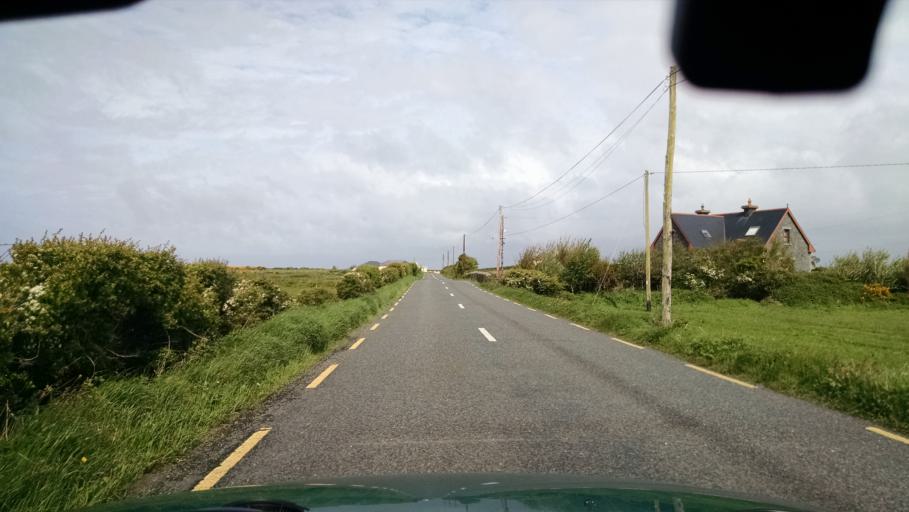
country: IE
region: Connaught
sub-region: County Galway
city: Bearna
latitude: 53.0118
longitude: -9.3674
